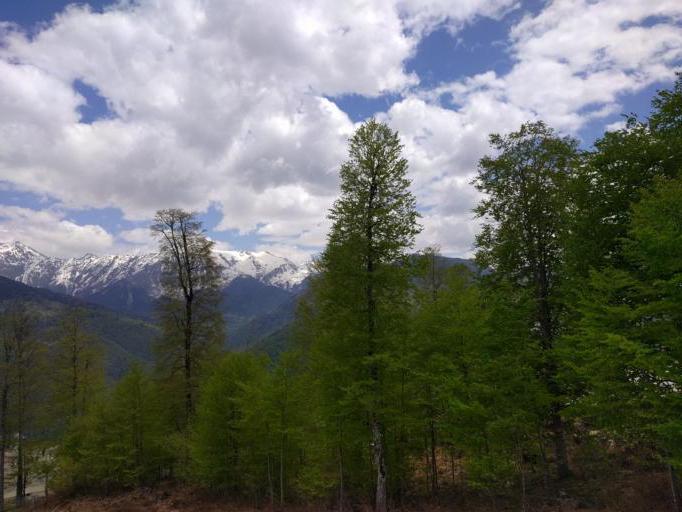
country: RU
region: Krasnodarskiy
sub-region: Sochi City
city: Krasnaya Polyana
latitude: 43.6568
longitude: 40.3190
